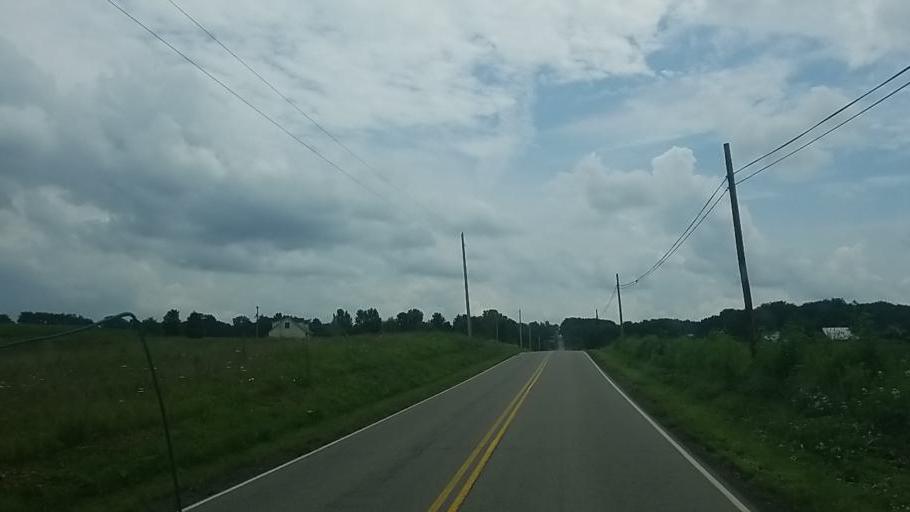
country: US
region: Ohio
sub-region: Licking County
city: Utica
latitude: 40.2293
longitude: -82.3654
